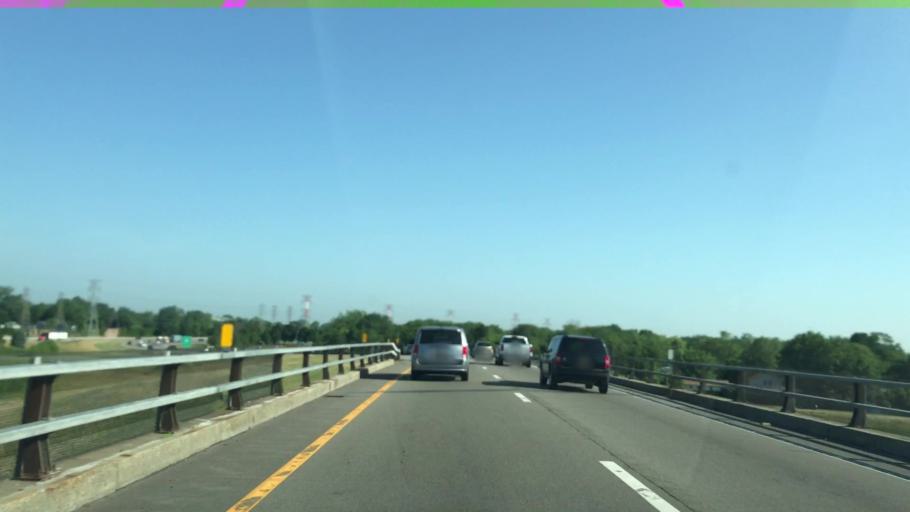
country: US
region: New York
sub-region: Erie County
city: Williamsville
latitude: 42.9498
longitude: -78.7630
